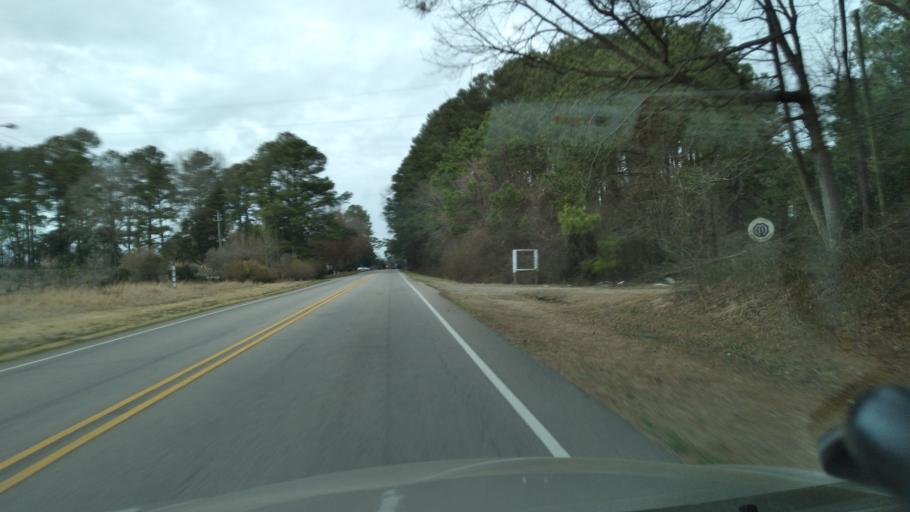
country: US
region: North Carolina
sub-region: Wake County
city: Garner
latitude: 35.6966
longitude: -78.6096
